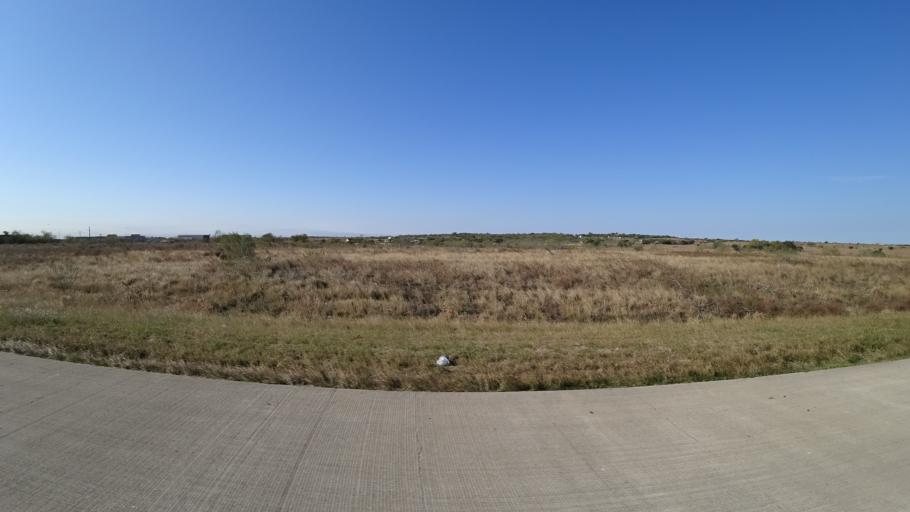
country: US
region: Texas
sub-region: Travis County
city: Onion Creek
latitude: 30.1271
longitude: -97.6634
